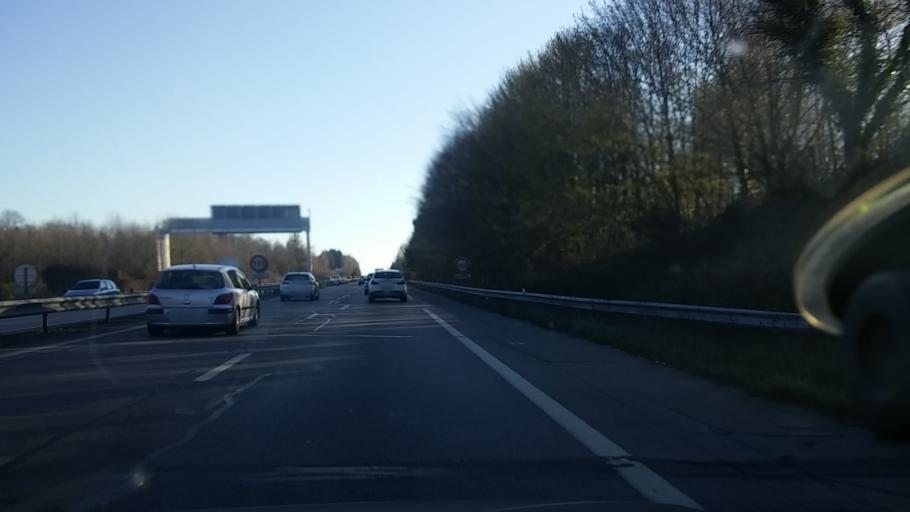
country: FR
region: Limousin
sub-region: Departement de la Haute-Vienne
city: Bonnac-la-Cote
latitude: 45.9240
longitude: 1.3014
